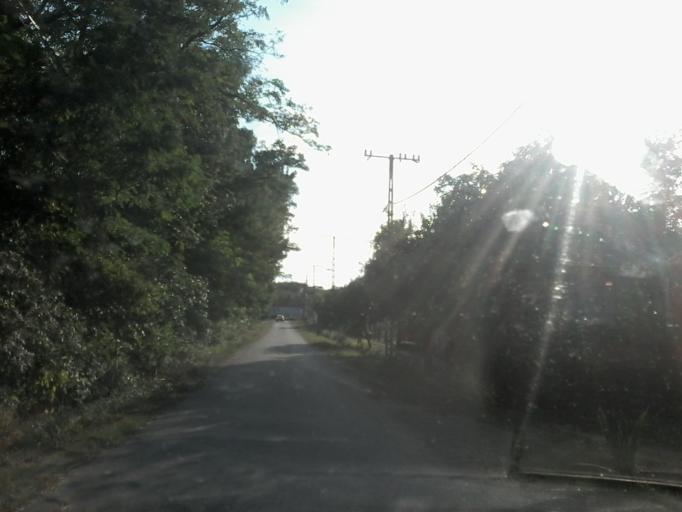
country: HU
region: Vas
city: Sarvar
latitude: 47.2195
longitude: 17.0164
